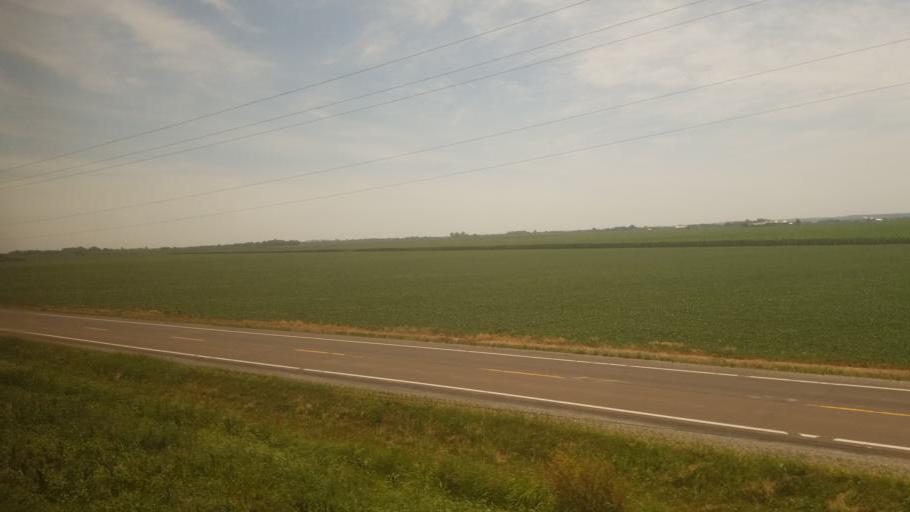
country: US
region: Missouri
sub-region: Carroll County
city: Carrollton
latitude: 39.3086
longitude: -93.6533
